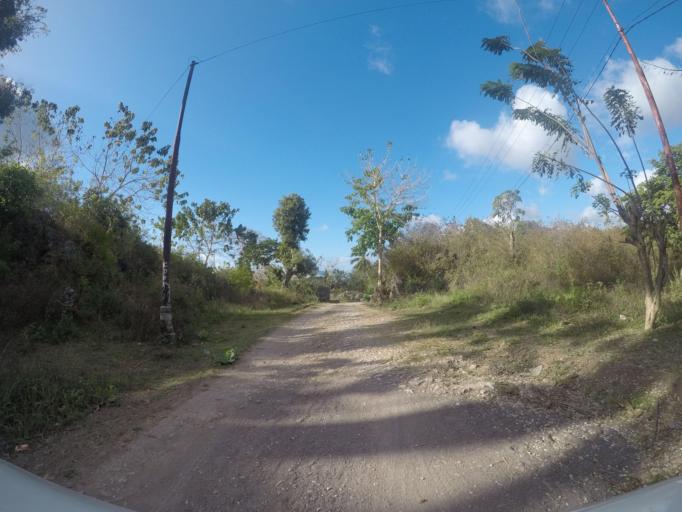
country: TL
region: Lautem
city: Lospalos
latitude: -8.4582
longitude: 126.8872
